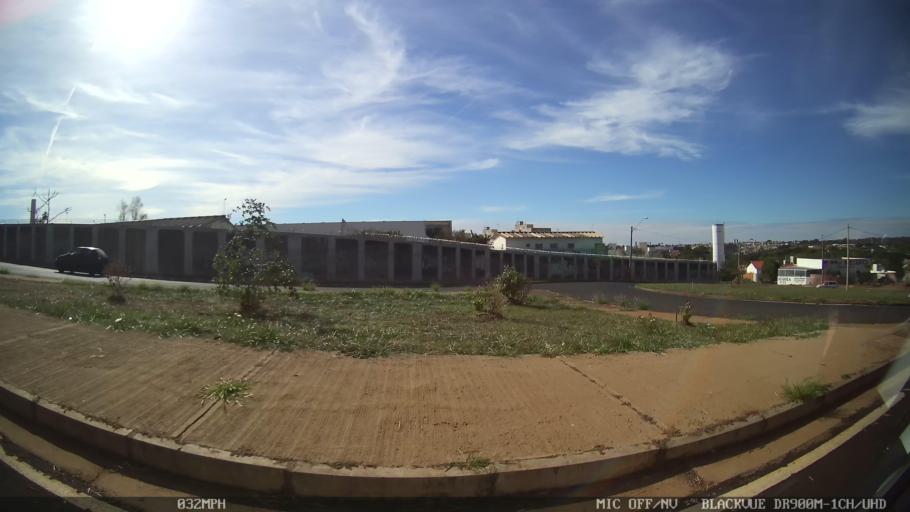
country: BR
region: Sao Paulo
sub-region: Sao Jose Do Rio Preto
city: Sao Jose do Rio Preto
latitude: -20.7898
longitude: -49.3512
